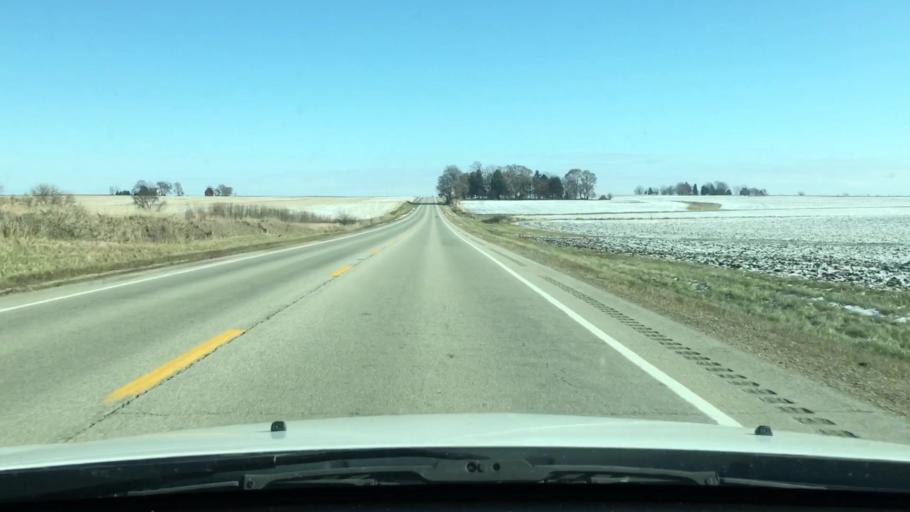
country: US
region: Illinois
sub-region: DeKalb County
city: Malta
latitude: 42.0010
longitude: -88.8907
